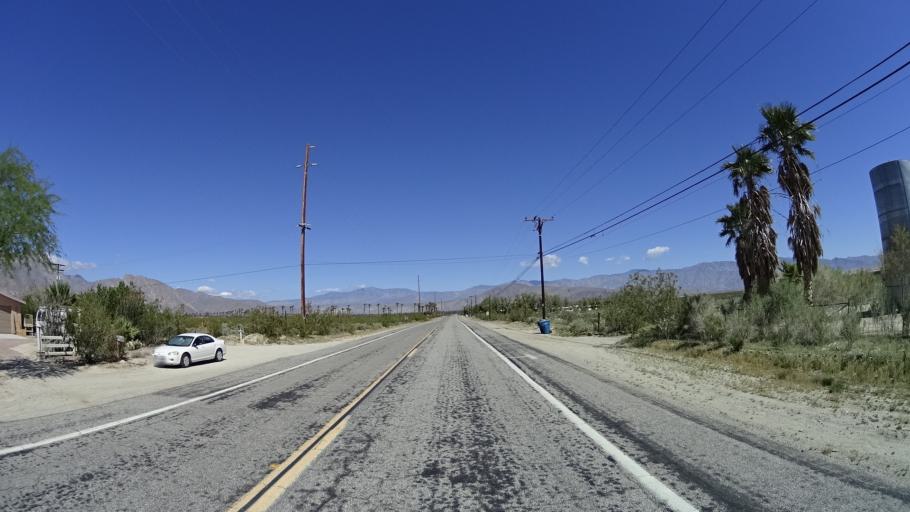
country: US
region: California
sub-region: San Diego County
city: Borrego Springs
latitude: 33.2276
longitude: -116.3478
